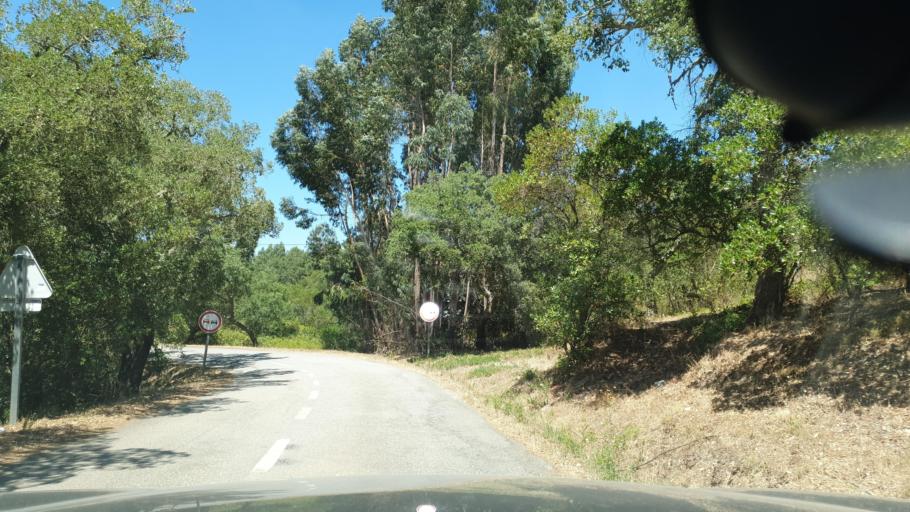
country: PT
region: Beja
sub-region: Odemira
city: Odemira
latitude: 37.6150
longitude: -8.5019
